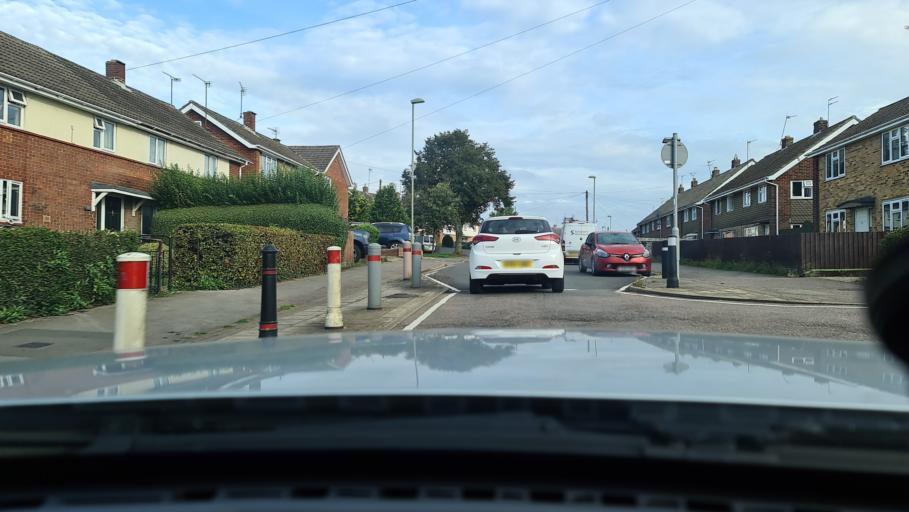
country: GB
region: England
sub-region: Oxfordshire
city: Banbury
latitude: 52.0646
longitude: -1.3647
